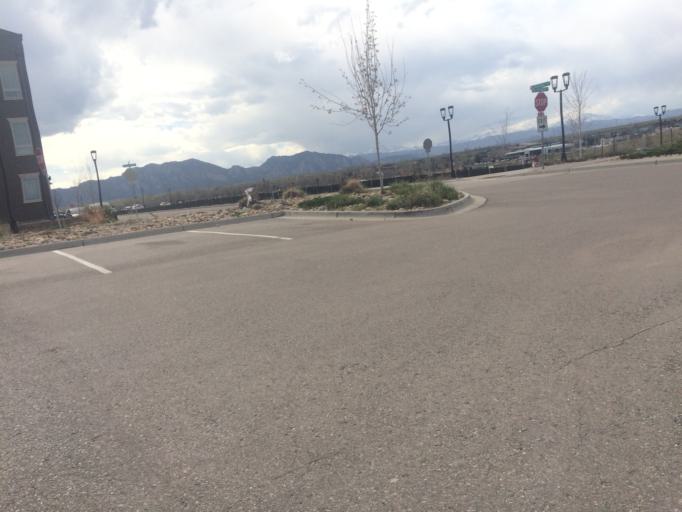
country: US
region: Colorado
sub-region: Boulder County
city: Superior
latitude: 39.9512
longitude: -105.1591
